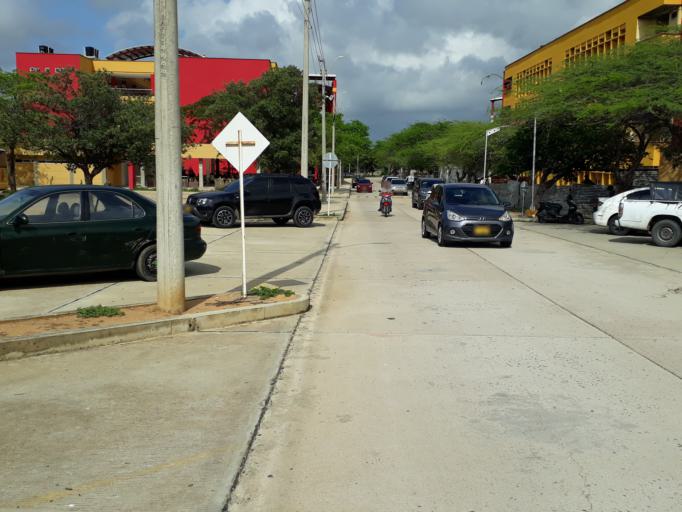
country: CO
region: La Guajira
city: Riohacha
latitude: 11.5116
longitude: -72.8699
